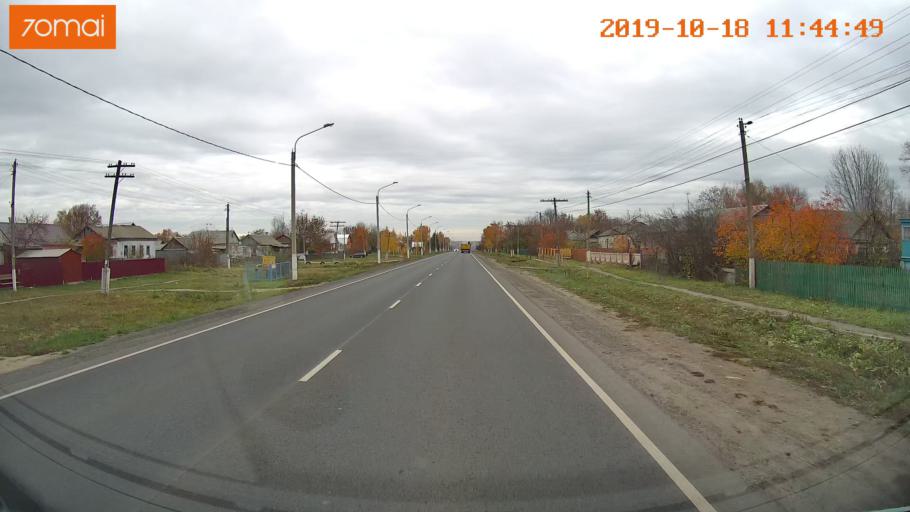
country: RU
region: Rjazan
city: Mikhaylov
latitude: 54.2053
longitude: 38.9624
